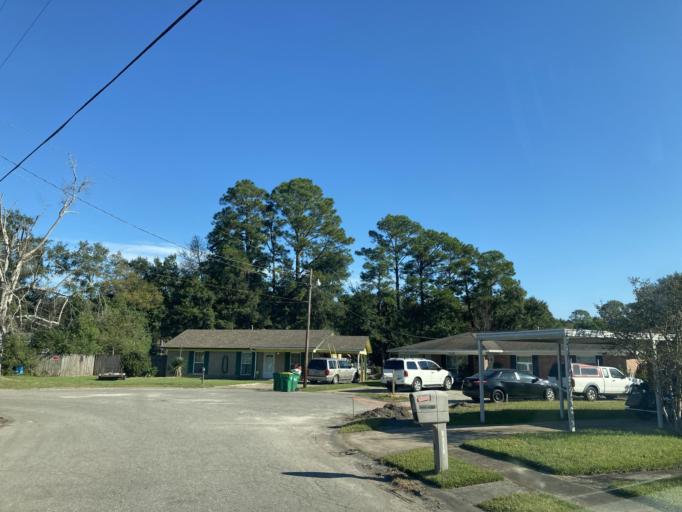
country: US
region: Mississippi
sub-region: Jackson County
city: Saint Martin
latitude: 30.4459
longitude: -88.8755
